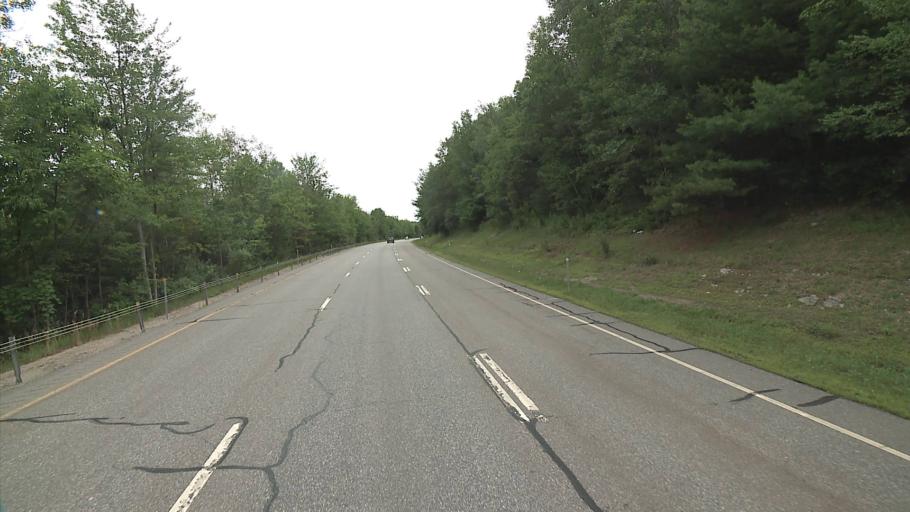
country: US
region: Connecticut
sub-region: Litchfield County
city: Torrington
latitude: 41.8495
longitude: -73.0928
